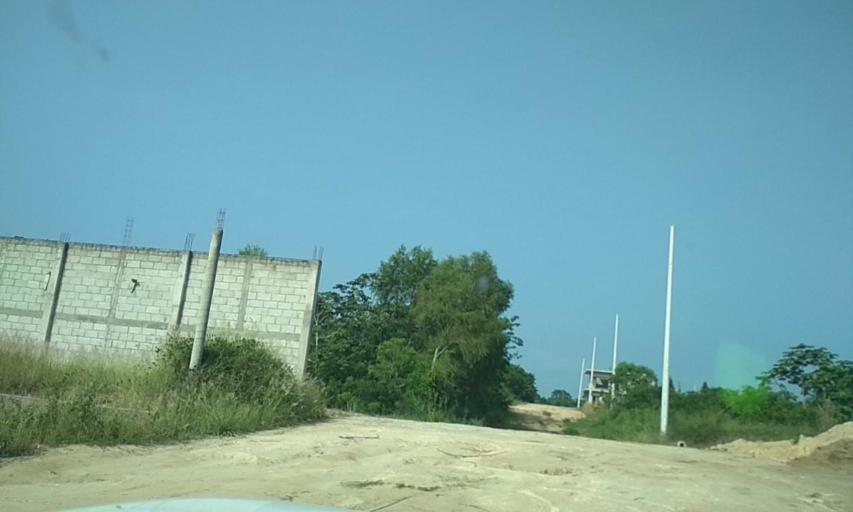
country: MX
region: Veracruz
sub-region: Martinez de la Torre
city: El Progreso
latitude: 20.1493
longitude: -97.0663
